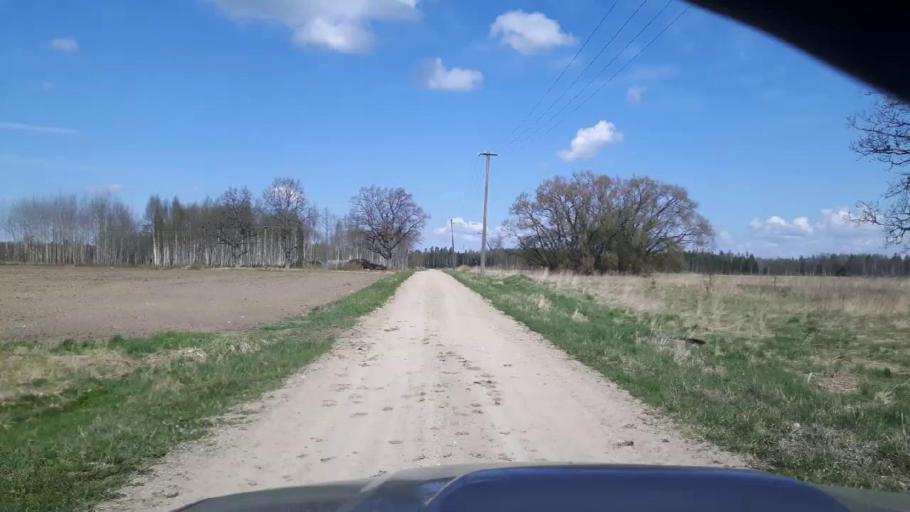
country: EE
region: Paernumaa
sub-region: Vaendra vald (alev)
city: Vandra
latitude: 58.5129
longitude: 25.0441
